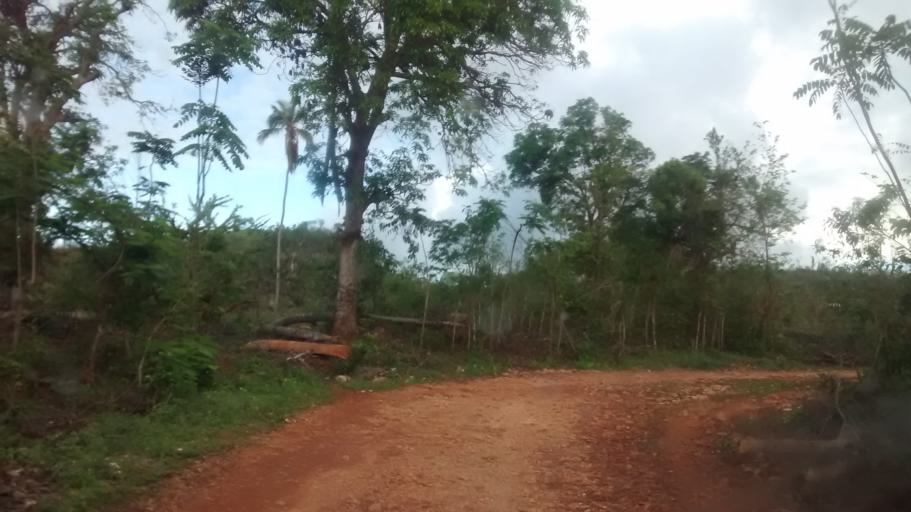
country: HT
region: Grandans
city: Corail
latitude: 18.5200
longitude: -73.7897
